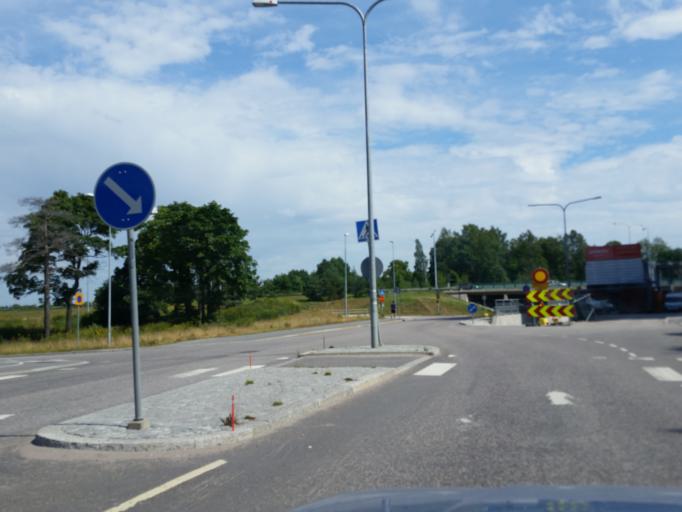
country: FI
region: Uusimaa
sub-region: Helsinki
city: Helsinki
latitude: 60.1651
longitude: 24.9085
